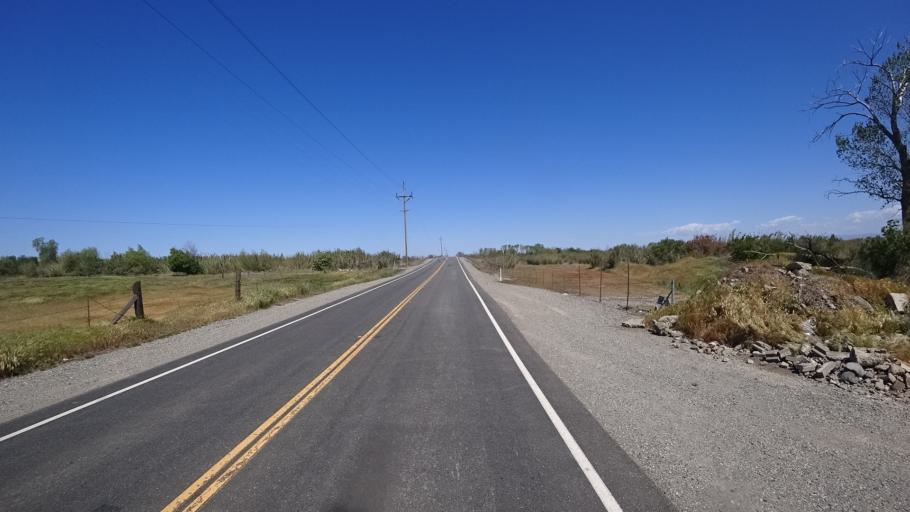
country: US
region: California
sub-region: Glenn County
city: Orland
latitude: 39.7571
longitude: -122.1410
